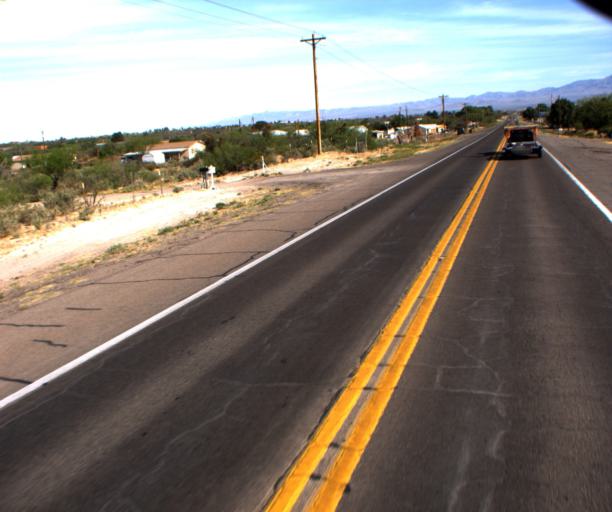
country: US
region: Arizona
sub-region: Graham County
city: Cactus Flat
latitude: 32.7556
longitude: -109.7163
